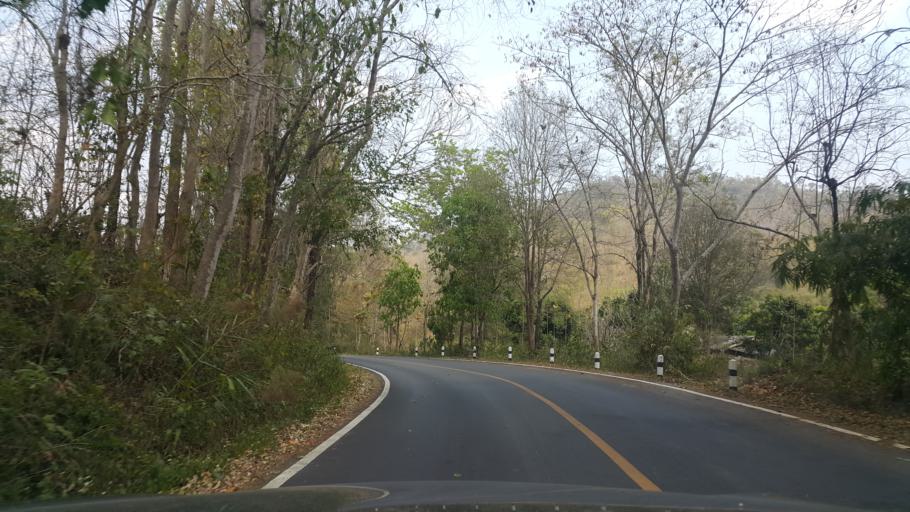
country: TH
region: Lamphun
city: Thung Hua Chang
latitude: 17.9013
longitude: 99.1123
